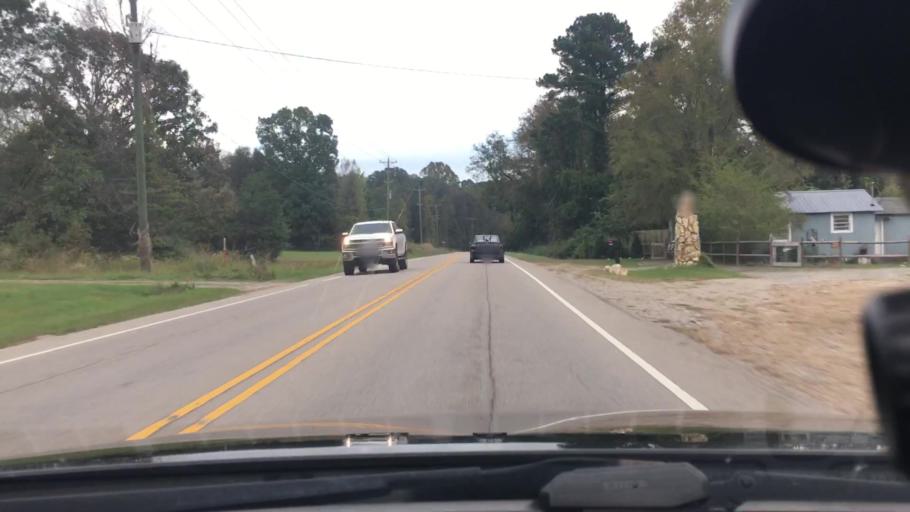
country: US
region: North Carolina
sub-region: Moore County
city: Robbins
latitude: 35.4042
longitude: -79.5720
